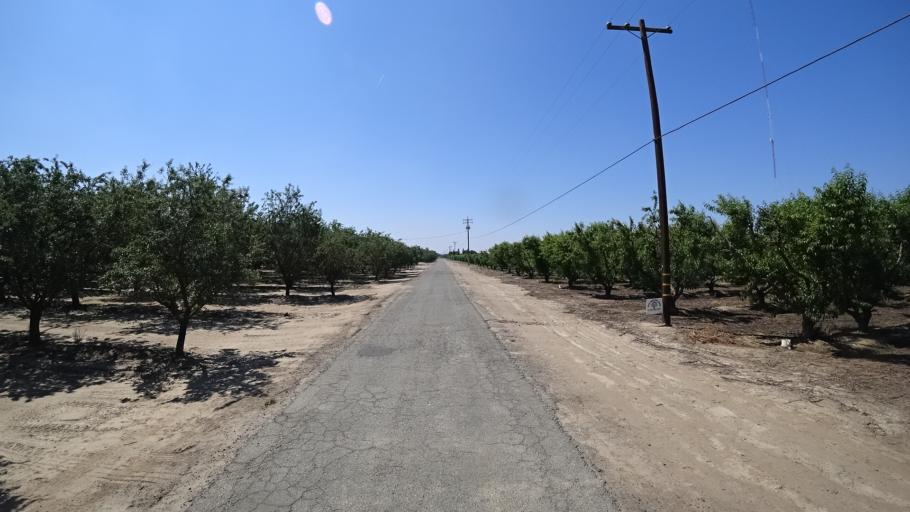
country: US
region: California
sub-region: Fresno County
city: Laton
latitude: 36.4485
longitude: -119.6184
